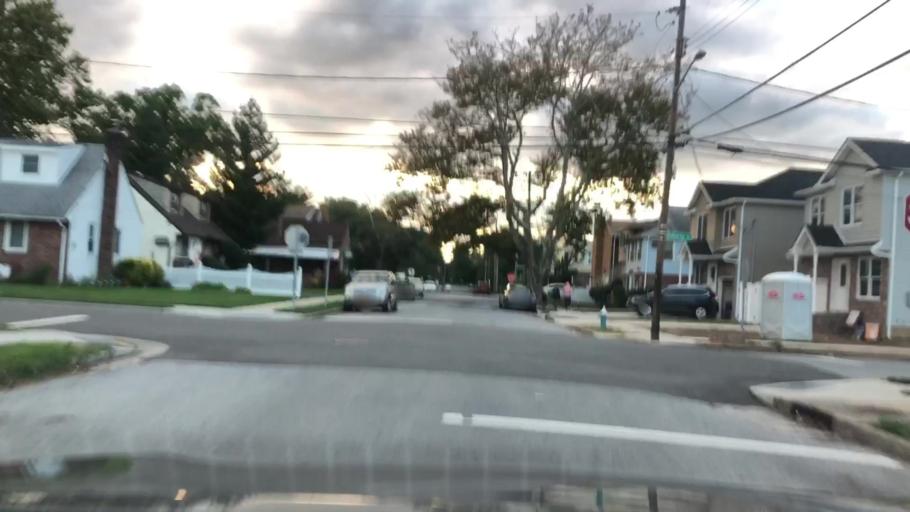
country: US
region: New York
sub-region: Nassau County
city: South Floral Park
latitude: 40.7000
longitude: -73.6962
